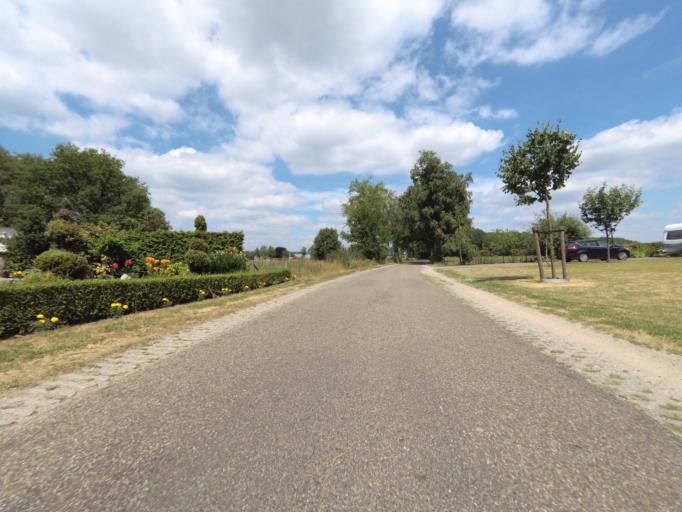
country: NL
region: Overijssel
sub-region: Gemeente Raalte
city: Raalte
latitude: 52.3125
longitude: 6.3004
